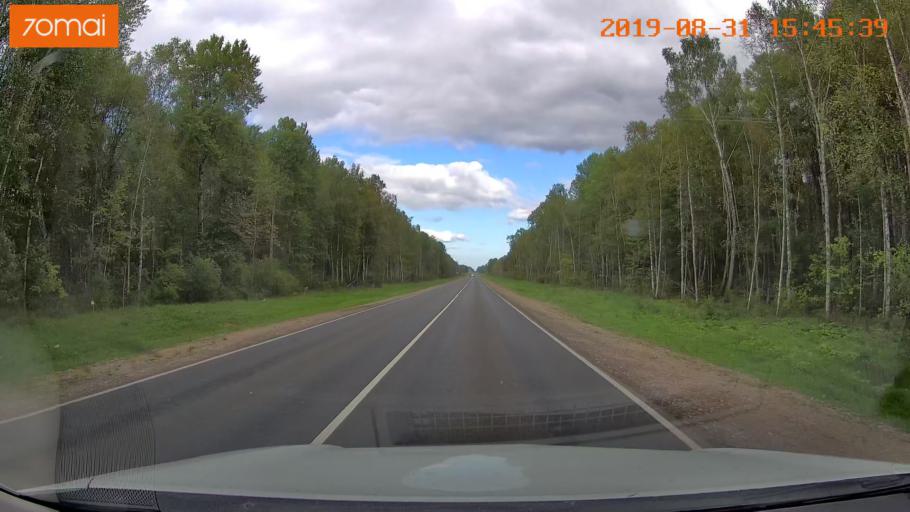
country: RU
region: Kaluga
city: Mosal'sk
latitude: 54.6678
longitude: 34.9647
